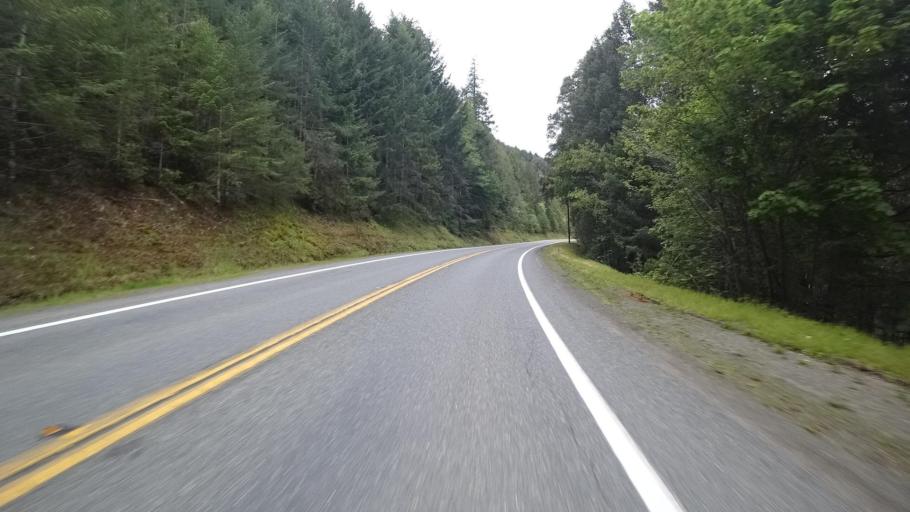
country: US
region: California
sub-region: Humboldt County
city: Willow Creek
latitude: 40.9985
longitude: -123.6403
